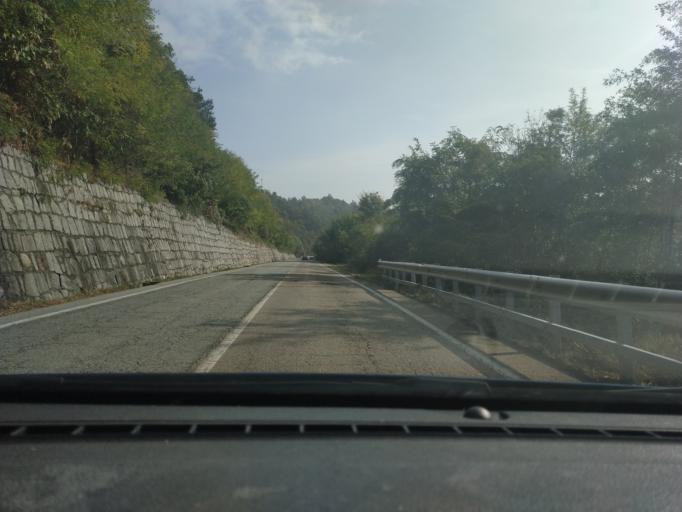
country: IT
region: Piedmont
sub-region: Provincia di Biella
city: Sala Biellese
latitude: 45.5222
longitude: 7.9475
